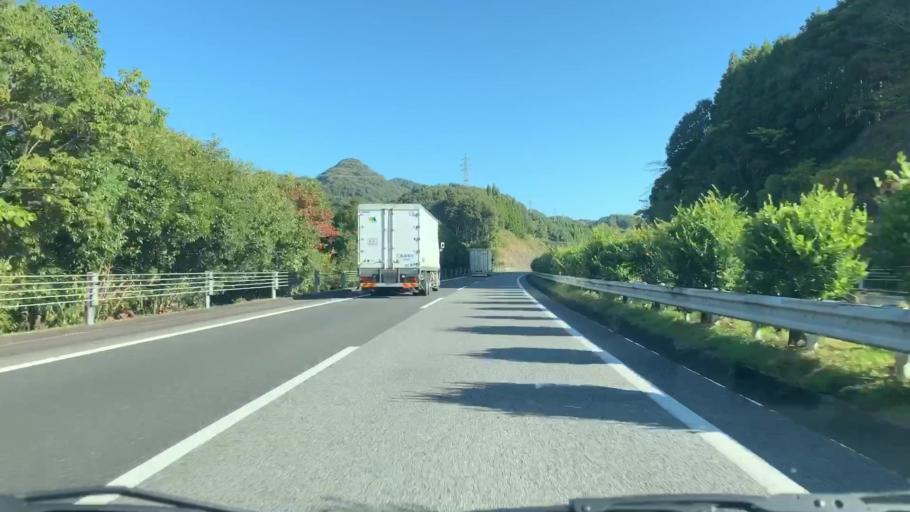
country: JP
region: Saga Prefecture
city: Takeocho-takeo
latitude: 33.2275
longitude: 130.0515
